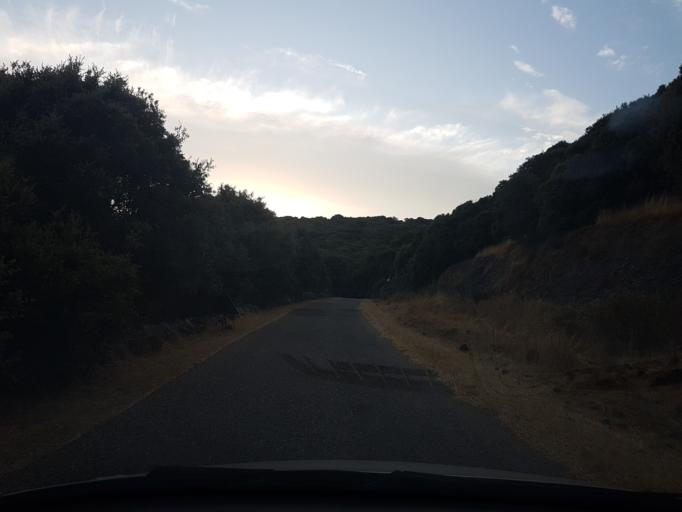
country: IT
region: Sardinia
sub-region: Provincia di Oristano
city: Seneghe
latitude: 40.1083
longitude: 8.6013
